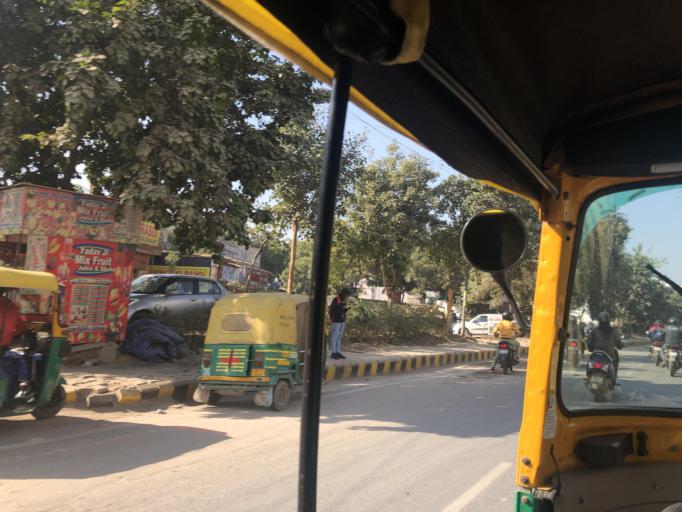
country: IN
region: Haryana
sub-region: Gurgaon
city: Gurgaon
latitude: 28.4495
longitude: 77.0708
